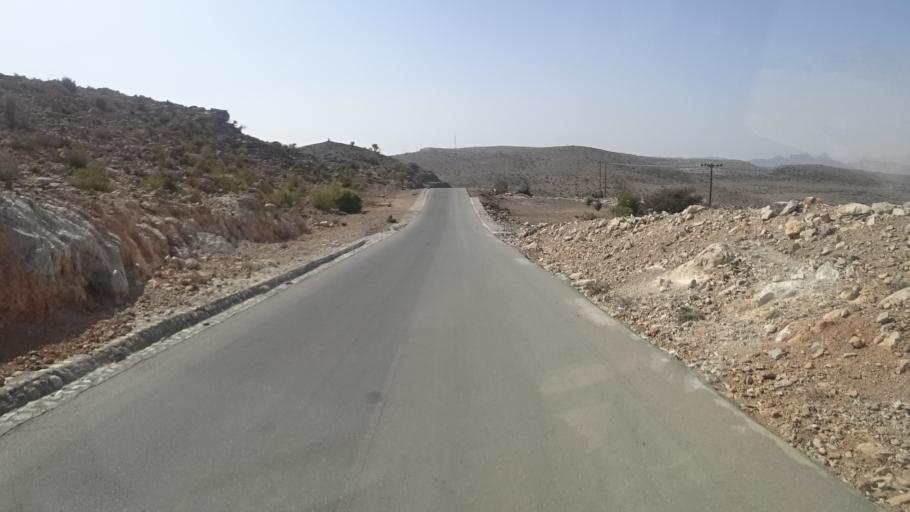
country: OM
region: Al Batinah
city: Rustaq
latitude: 23.2325
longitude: 57.1985
